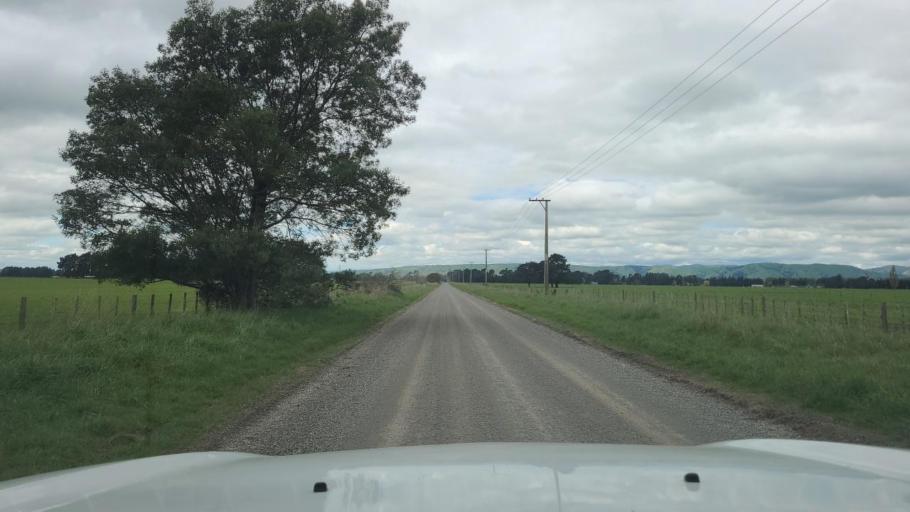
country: NZ
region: Wellington
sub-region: Masterton District
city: Masterton
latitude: -41.1189
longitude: 175.4139
